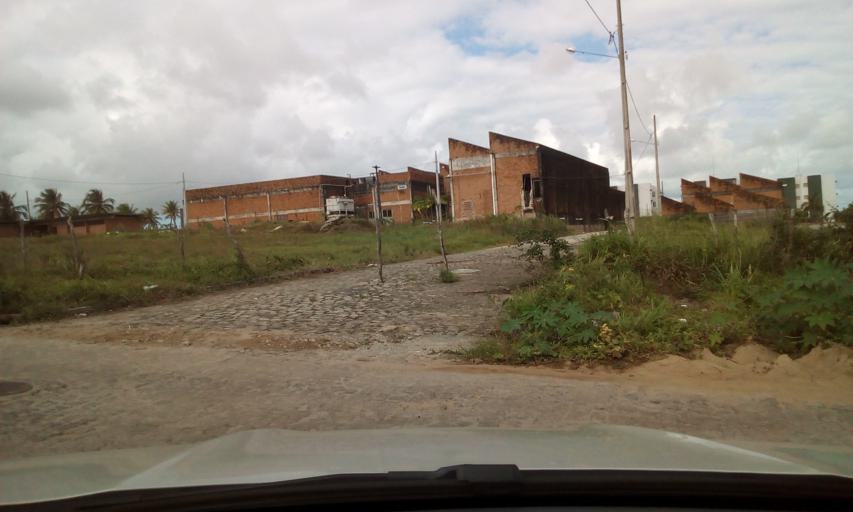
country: BR
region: Paraiba
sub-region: Joao Pessoa
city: Joao Pessoa
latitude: -7.1879
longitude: -34.8788
